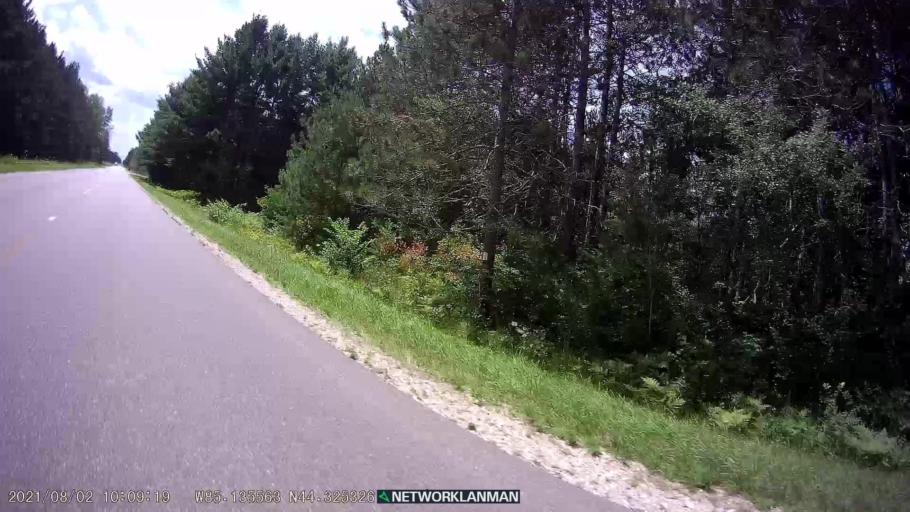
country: US
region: Michigan
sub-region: Missaukee County
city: Lake City
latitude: 44.3252
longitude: -85.1356
